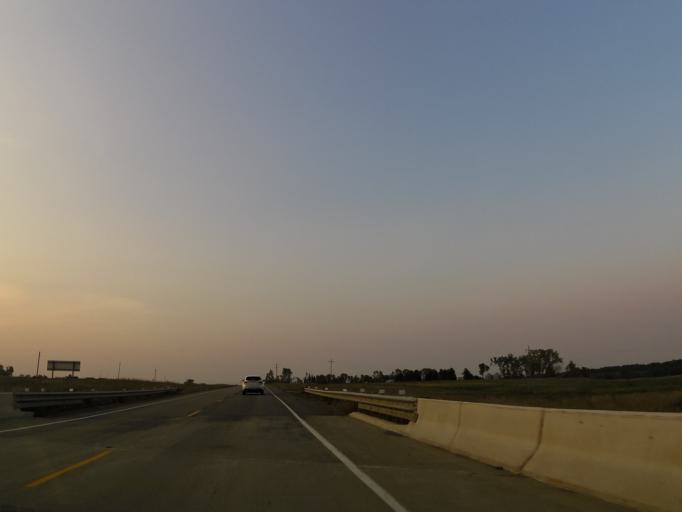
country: US
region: North Dakota
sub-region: Walsh County
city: Park River
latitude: 48.1808
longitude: -97.6232
